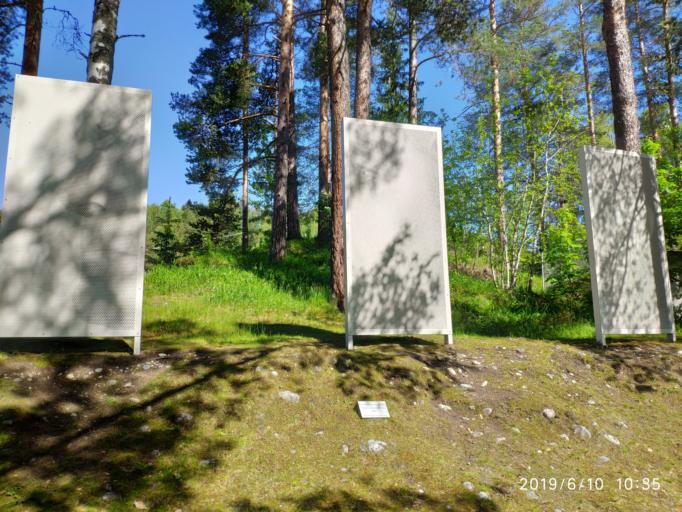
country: NO
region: Oppland
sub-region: Jevnaker
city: Jevnaker
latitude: 60.2220
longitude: 10.3696
